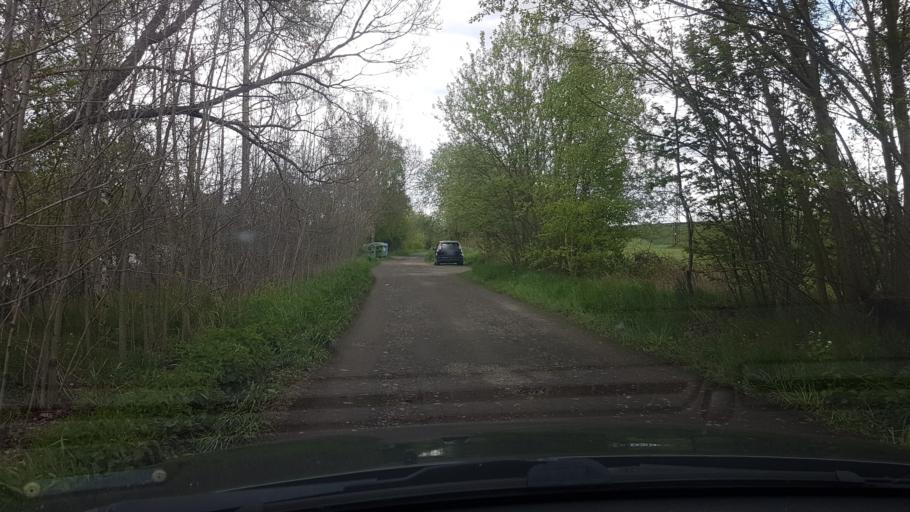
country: CZ
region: Karlovarsky
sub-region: Okres Cheb
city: Cheb
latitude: 50.0561
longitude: 12.3864
